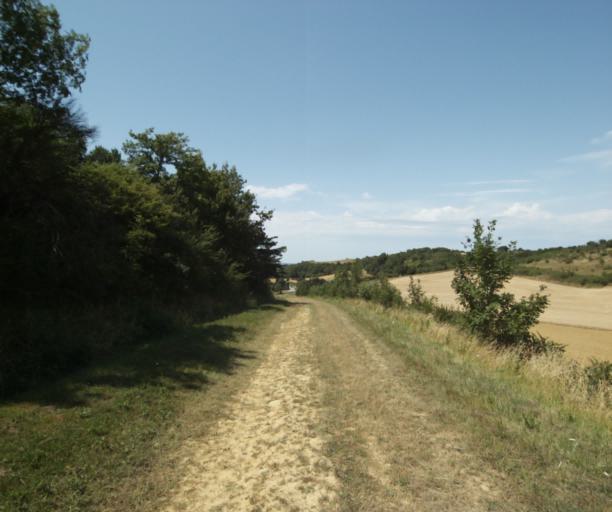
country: FR
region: Midi-Pyrenees
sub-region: Departement de la Haute-Garonne
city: Saint-Felix-Lauragais
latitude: 43.4424
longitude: 1.8752
